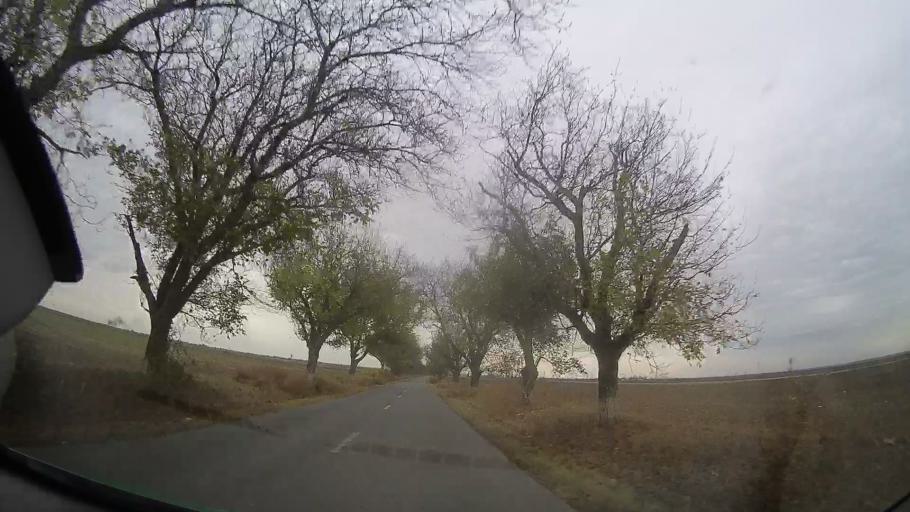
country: RO
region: Prahova
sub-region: Comuna Fantanele
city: Fantanele
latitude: 45.0142
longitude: 26.4073
